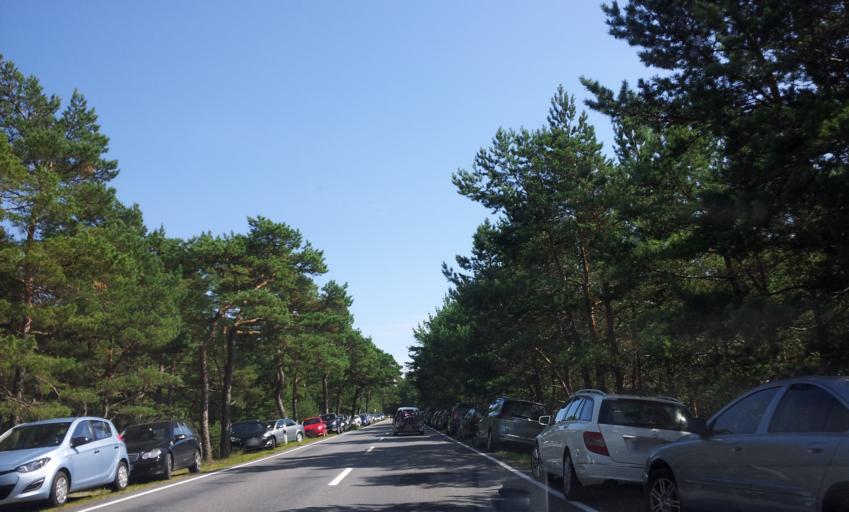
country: DE
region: Mecklenburg-Vorpommern
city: Glowe
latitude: 54.5877
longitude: 13.3992
